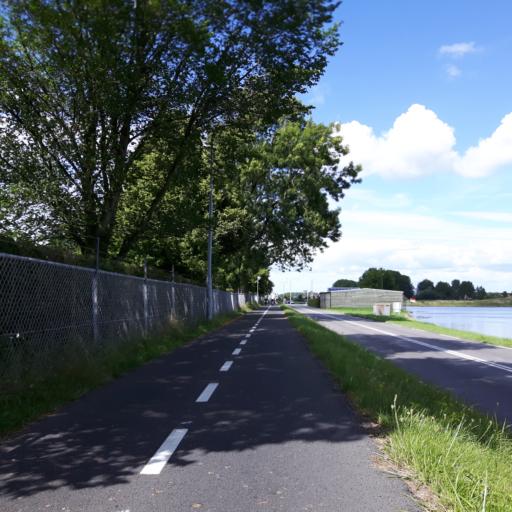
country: NL
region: Zeeland
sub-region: Gemeente Goes
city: Goes
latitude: 51.5170
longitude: 3.8914
